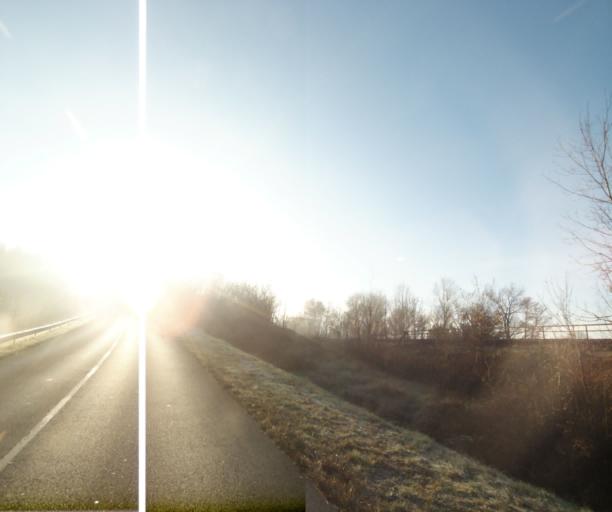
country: FR
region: Poitou-Charentes
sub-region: Departement de la Charente-Maritime
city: Bussac-sur-Charente
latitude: 45.7763
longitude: -0.6247
